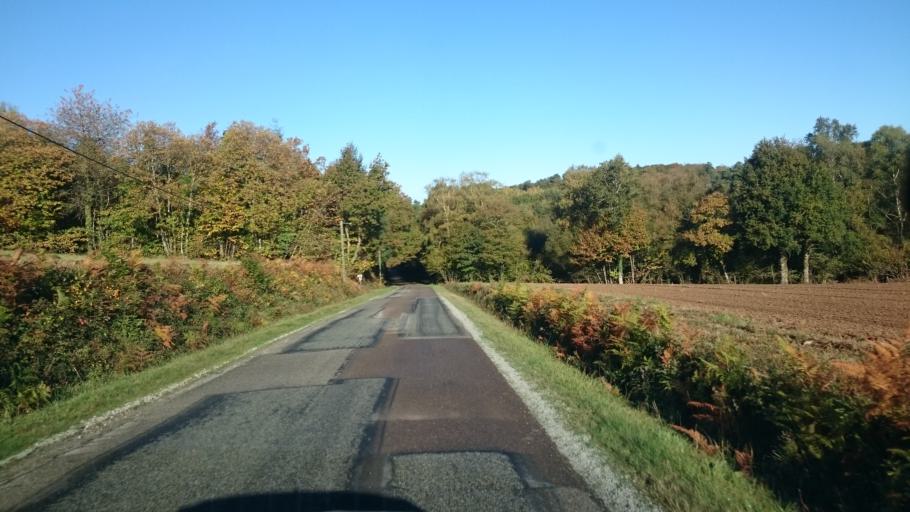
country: FR
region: Brittany
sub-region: Departement d'Ille-et-Vilaine
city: Laille
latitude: 47.9613
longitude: -1.7039
